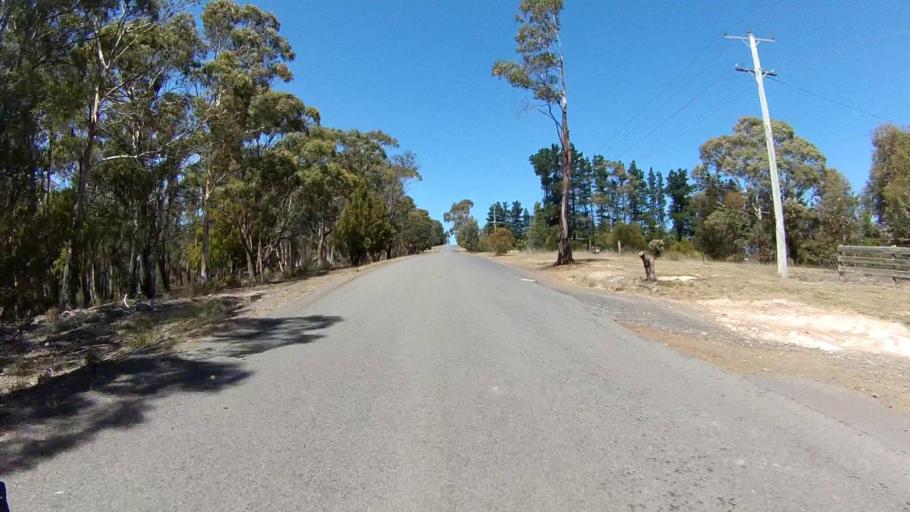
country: AU
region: Tasmania
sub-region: Clarence
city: Cambridge
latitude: -42.8448
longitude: 147.4236
